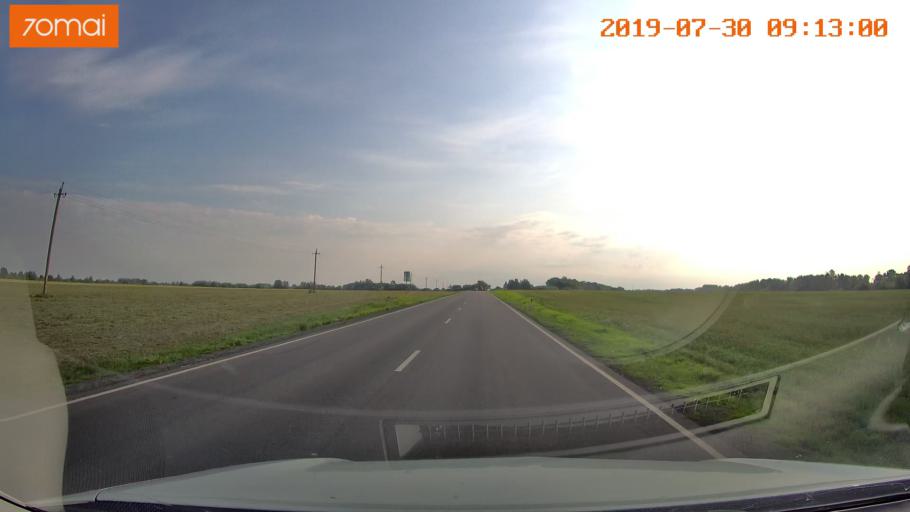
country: RU
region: Kaliningrad
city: Nesterov
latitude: 54.6216
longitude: 22.4880
